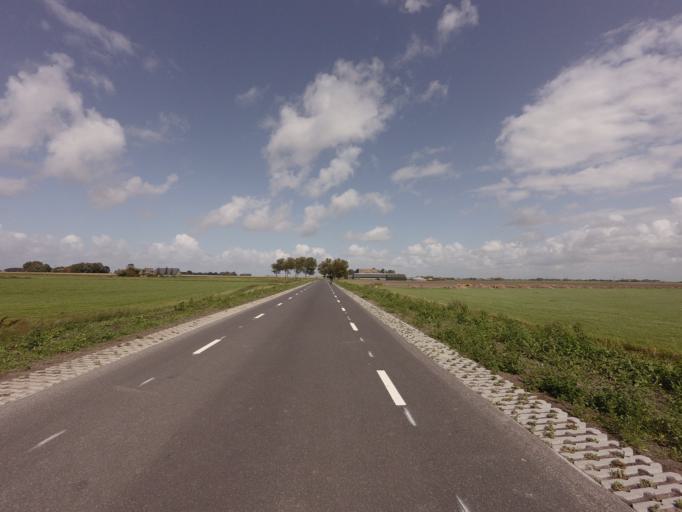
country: NL
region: Friesland
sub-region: Gemeente Harlingen
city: Harlingen
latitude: 53.1519
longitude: 5.4774
